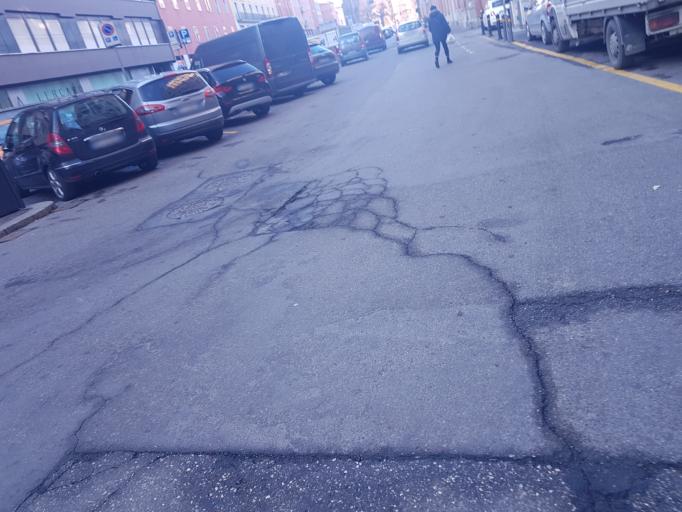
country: IT
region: Emilia-Romagna
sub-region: Provincia di Bologna
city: Bologna
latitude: 44.4987
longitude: 11.3379
